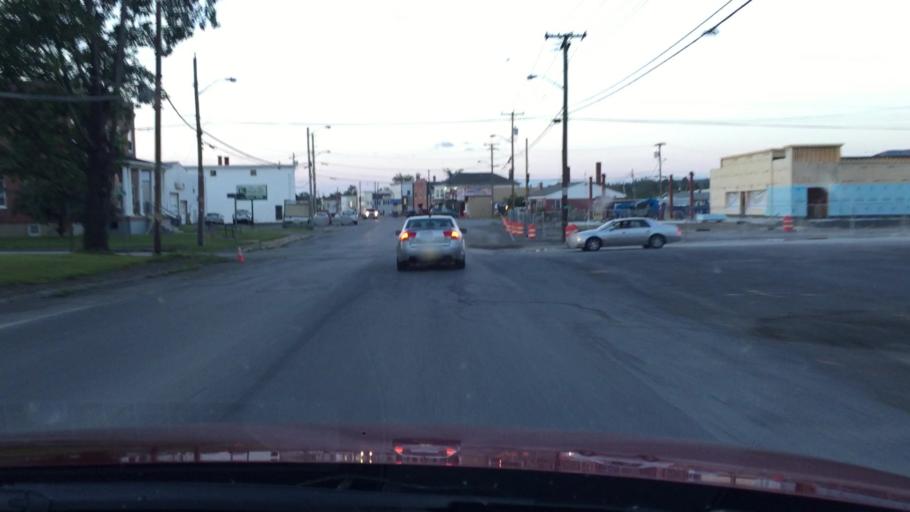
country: US
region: Maine
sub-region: Aroostook County
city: Easton
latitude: 46.5129
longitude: -67.8672
